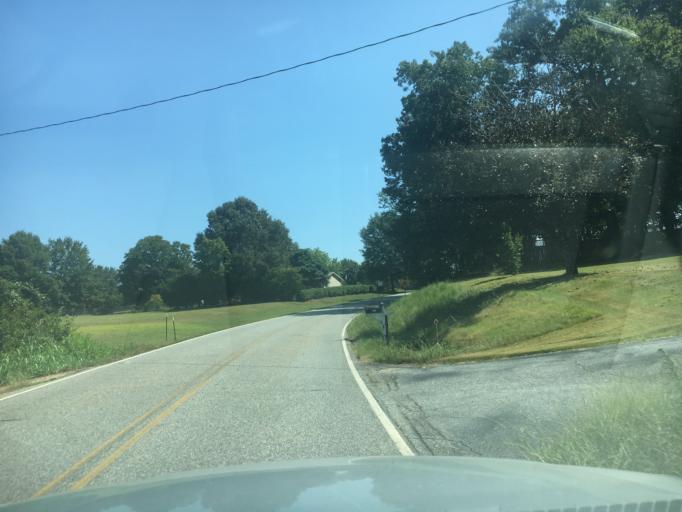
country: US
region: South Carolina
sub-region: Spartanburg County
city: Boiling Springs
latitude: 35.1242
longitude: -82.0329
